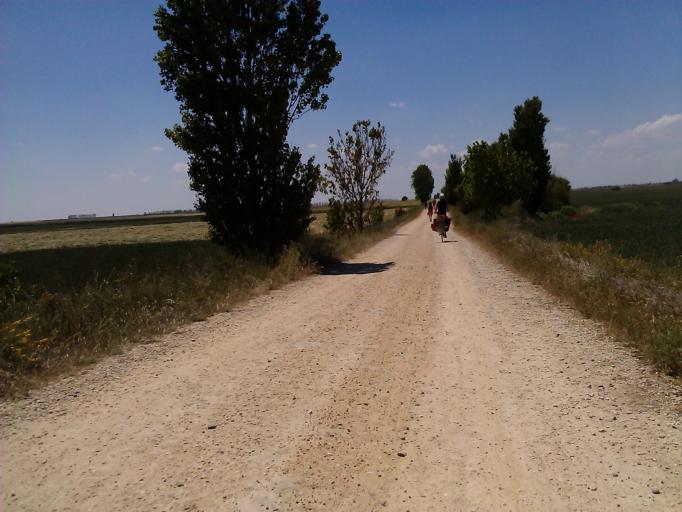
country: ES
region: Castille and Leon
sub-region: Provincia de Palencia
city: Bustillo del Paramo de Carrion
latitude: 42.3373
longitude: -4.7247
